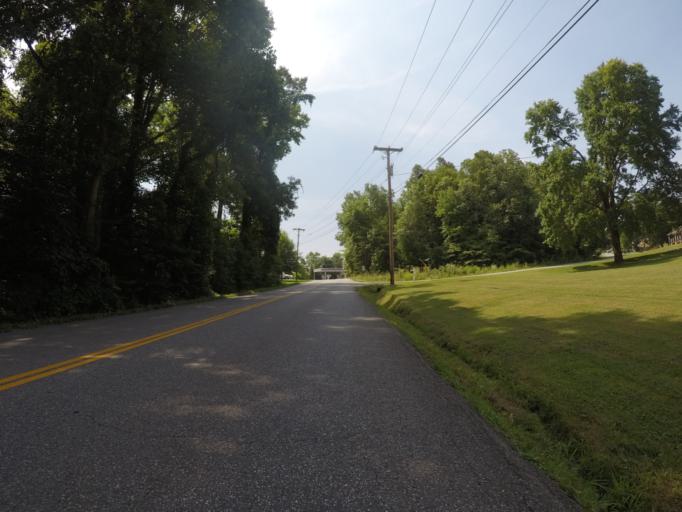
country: US
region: Kentucky
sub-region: Boyd County
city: Ironville
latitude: 38.4419
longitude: -82.7083
